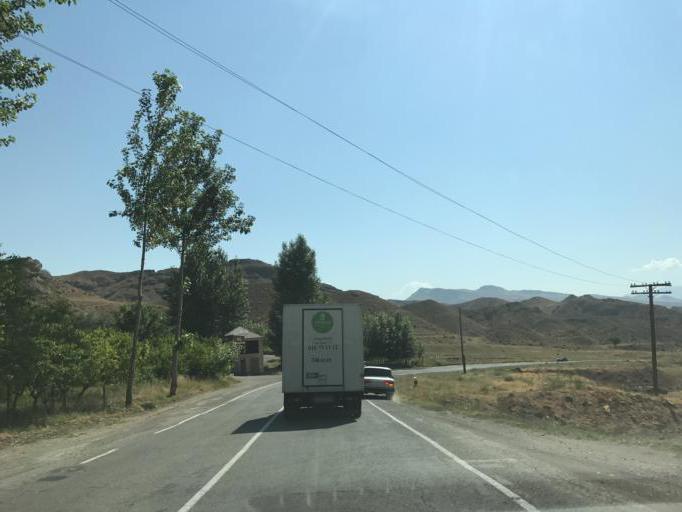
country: AM
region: Vayots' Dzori Marz
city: Yeghegnadzor
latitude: 39.7575
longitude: 45.3475
